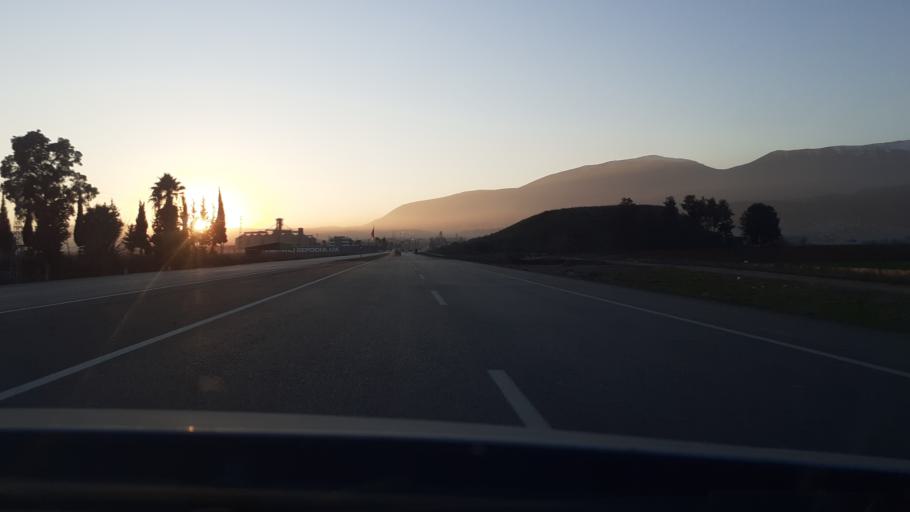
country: TR
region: Hatay
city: Kirikhan
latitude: 36.5029
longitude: 36.3960
